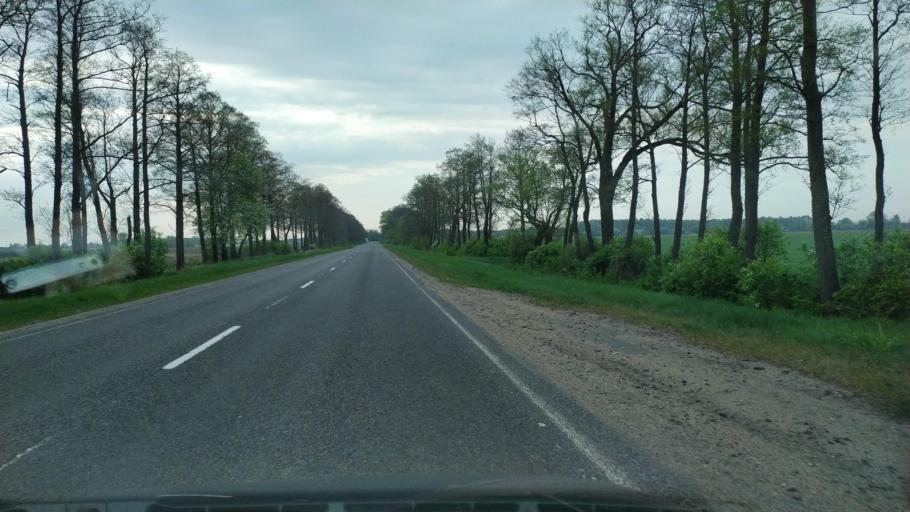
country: BY
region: Brest
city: Zhabinka
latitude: 52.3051
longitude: 23.9279
